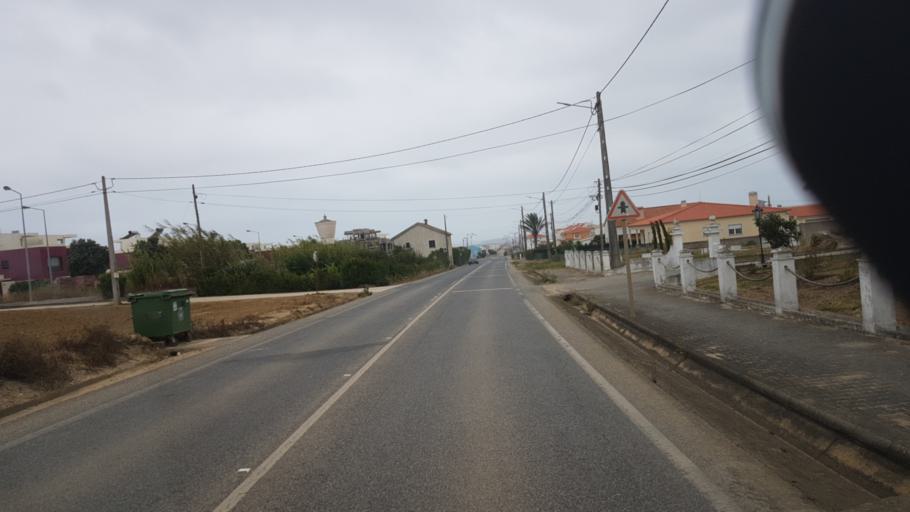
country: PT
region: Leiria
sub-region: Peniche
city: Atouguia da Baleia
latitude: 39.3359
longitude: -9.3088
